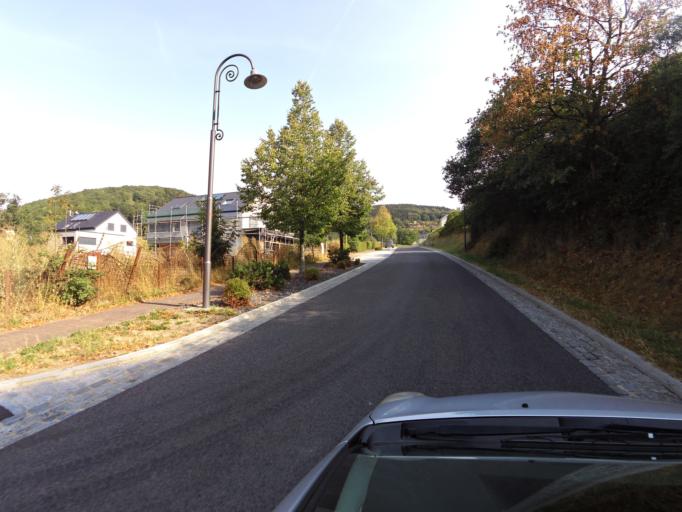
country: LU
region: Diekirch
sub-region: Canton de Diekirch
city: Bourscheid
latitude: 49.9152
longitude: 6.0826
